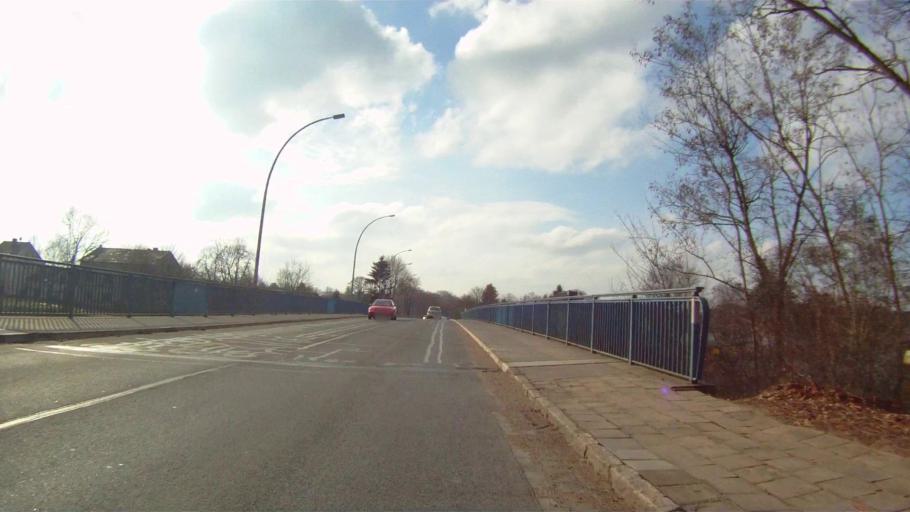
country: DE
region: Berlin
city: Muggelheim
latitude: 52.3727
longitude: 13.7080
